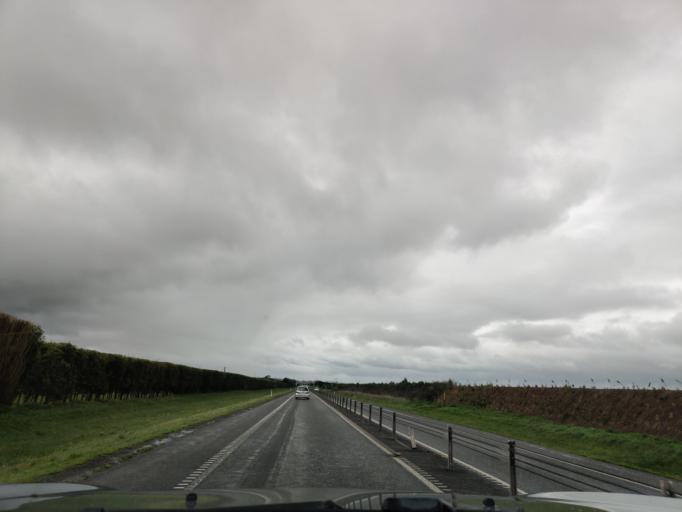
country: NZ
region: Hawke's Bay
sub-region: Hastings District
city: Hastings
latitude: -39.6178
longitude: 176.8204
